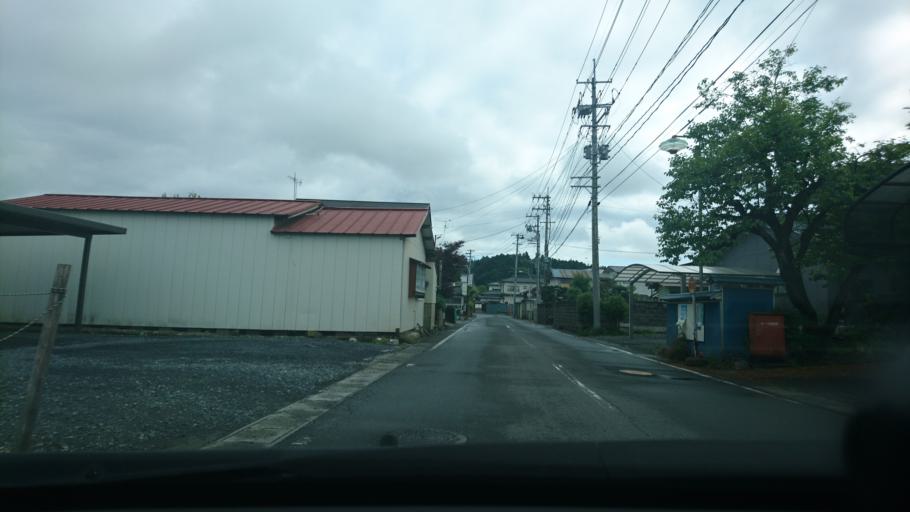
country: JP
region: Miyagi
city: Wakuya
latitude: 38.6535
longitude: 141.2765
